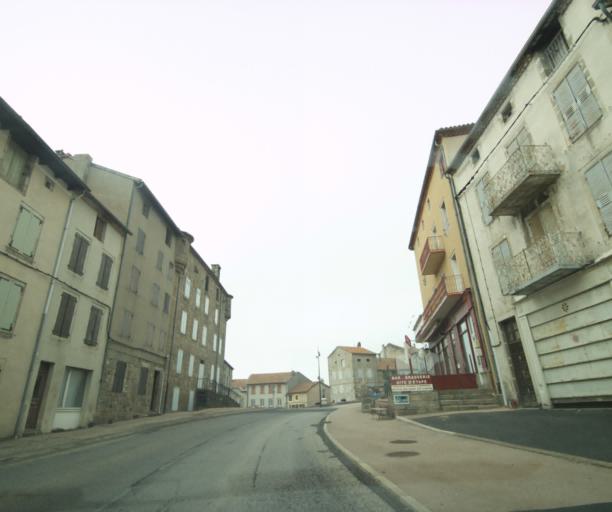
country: FR
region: Languedoc-Roussillon
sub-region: Departement de la Lozere
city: Langogne
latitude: 44.7694
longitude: 3.8835
